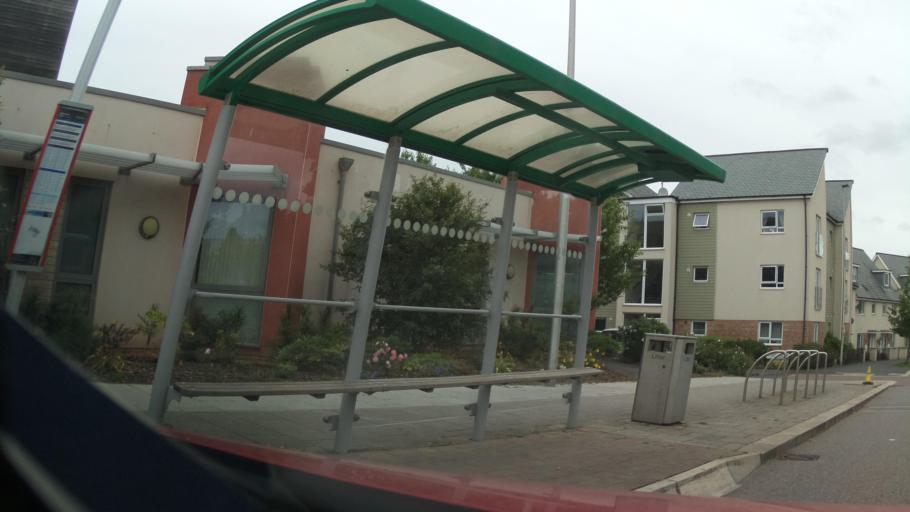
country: GB
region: England
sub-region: Devon
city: Topsham
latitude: 50.7480
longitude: -3.4150
